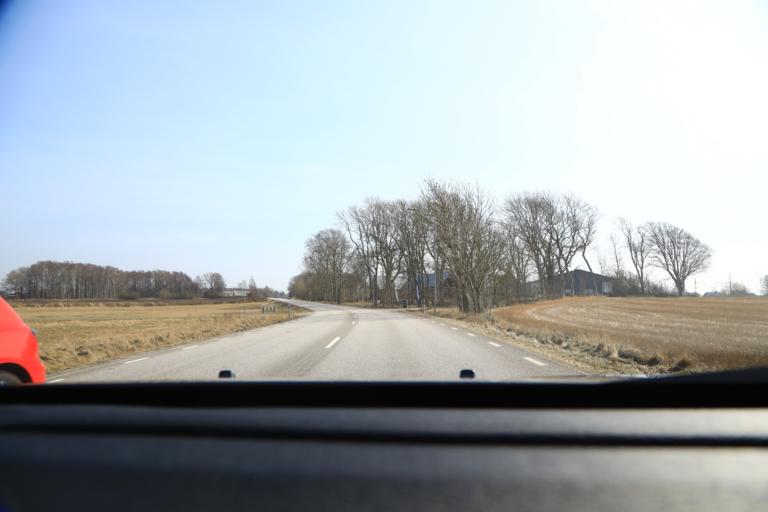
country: SE
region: Halland
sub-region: Kungsbacka Kommun
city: Frillesas
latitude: 57.2470
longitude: 12.1839
